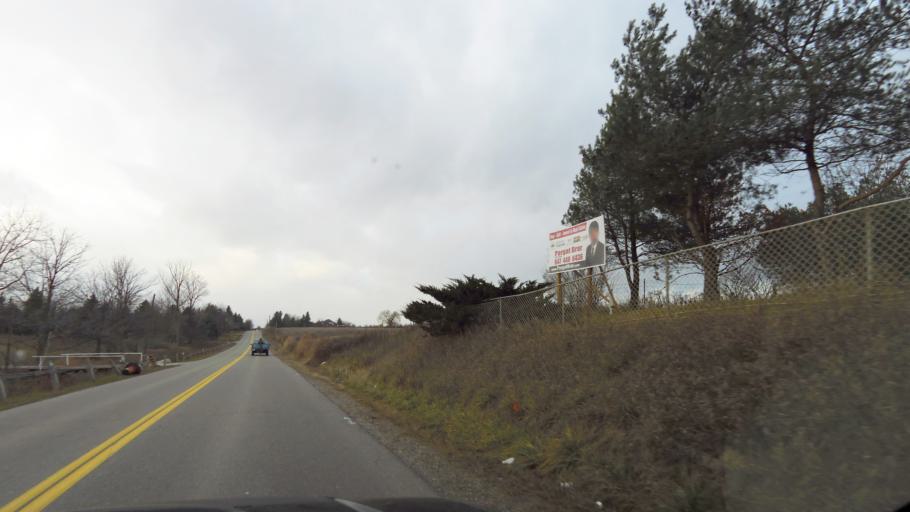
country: CA
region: Ontario
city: Brampton
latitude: 43.8151
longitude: -79.6975
